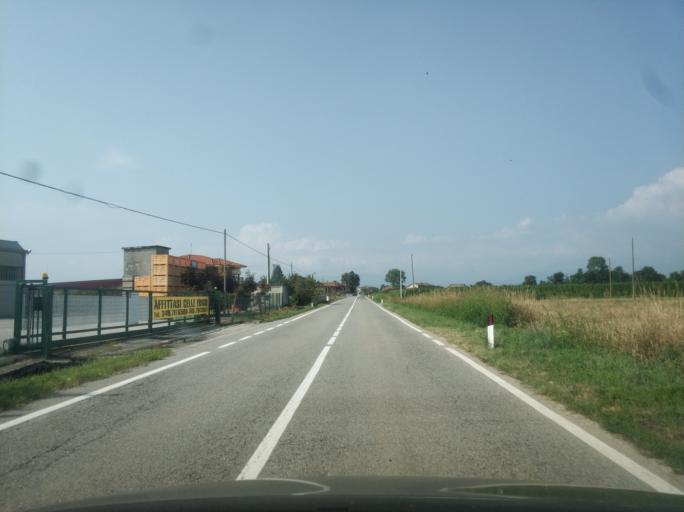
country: IT
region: Piedmont
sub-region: Provincia di Cuneo
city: Tarantasca
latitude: 44.4930
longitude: 7.5571
